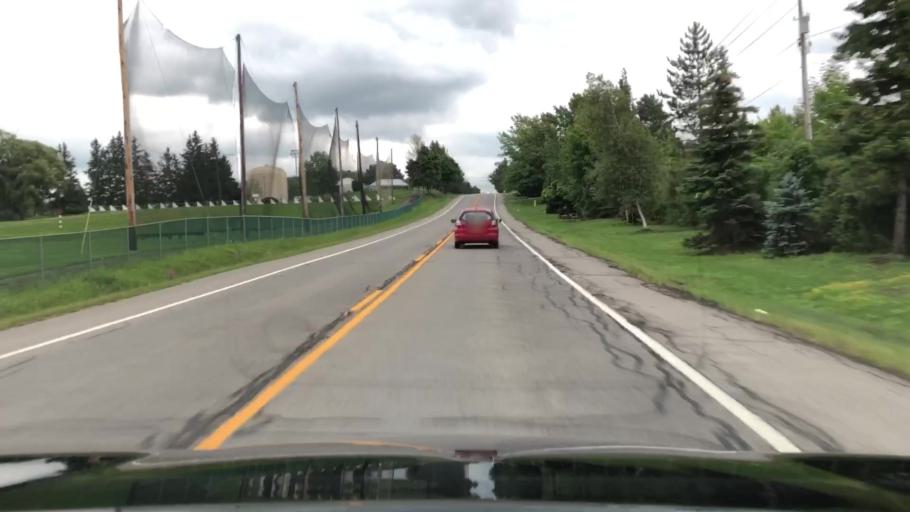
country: US
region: New York
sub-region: Erie County
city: Orchard Park
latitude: 42.7744
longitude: -78.6968
